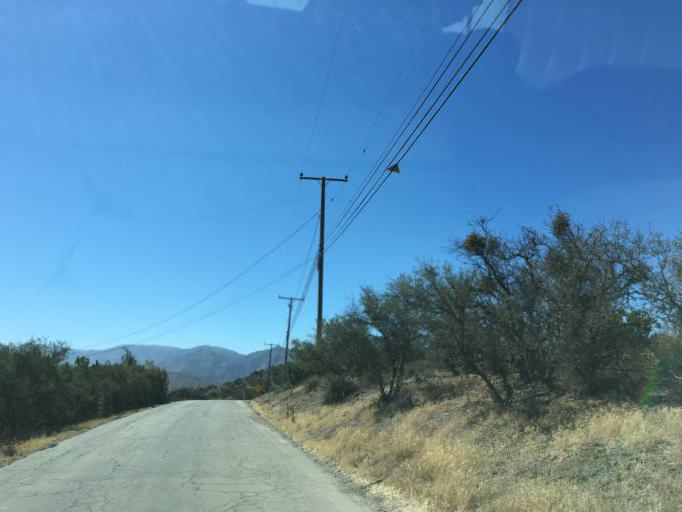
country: US
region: California
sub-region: Los Angeles County
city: Agua Dulce
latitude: 34.4752
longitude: -118.3483
